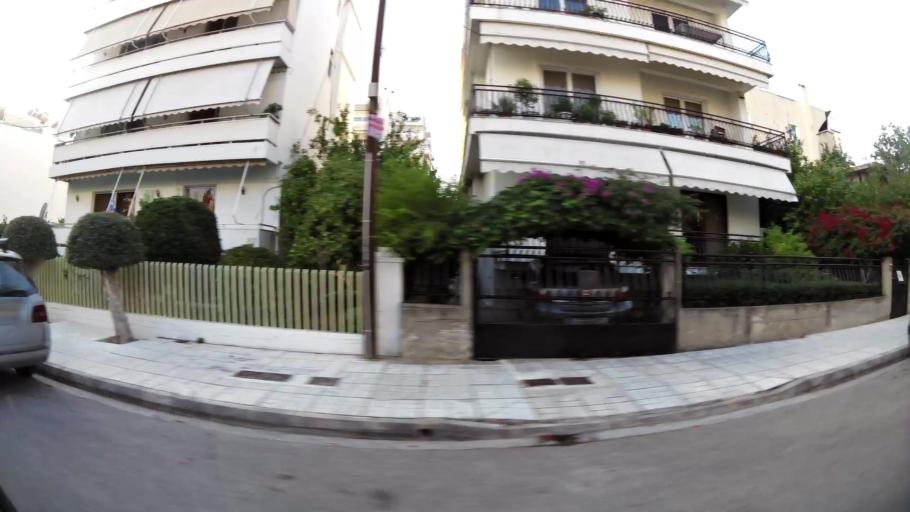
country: GR
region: Attica
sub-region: Nomarchia Athinas
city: Argyroupoli
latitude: 37.8956
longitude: 23.7683
